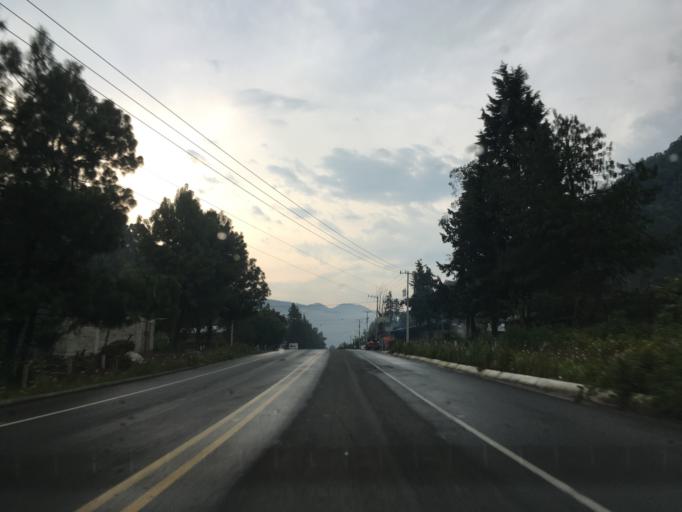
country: MX
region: Michoacan
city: Capacuaro
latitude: 19.5161
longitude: -102.1143
